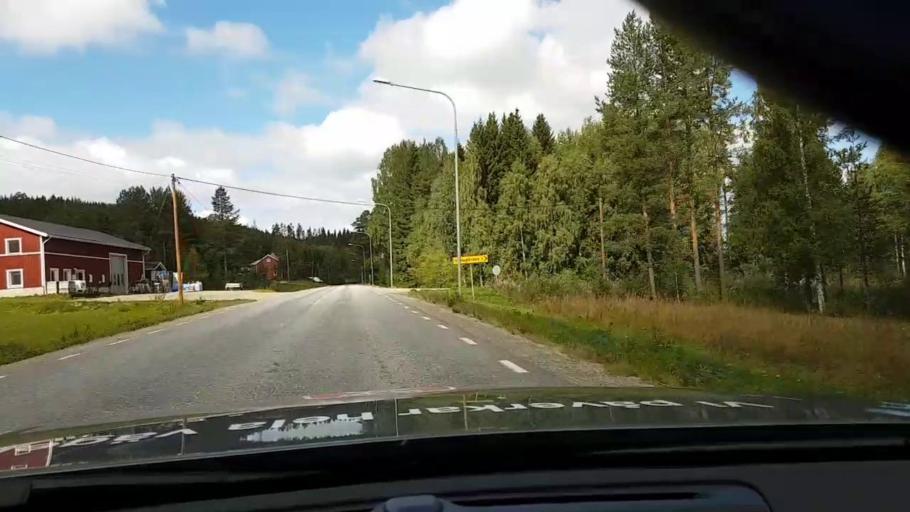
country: SE
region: Vaesternorrland
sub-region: OErnskoeldsviks Kommun
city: Bredbyn
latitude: 63.4895
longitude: 18.0828
